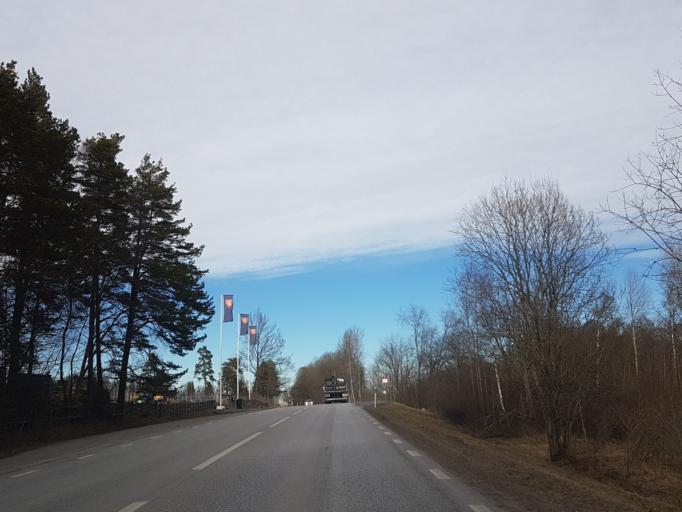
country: SE
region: Stockholm
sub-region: Norrtalje Kommun
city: Norrtalje
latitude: 59.7328
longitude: 18.6830
